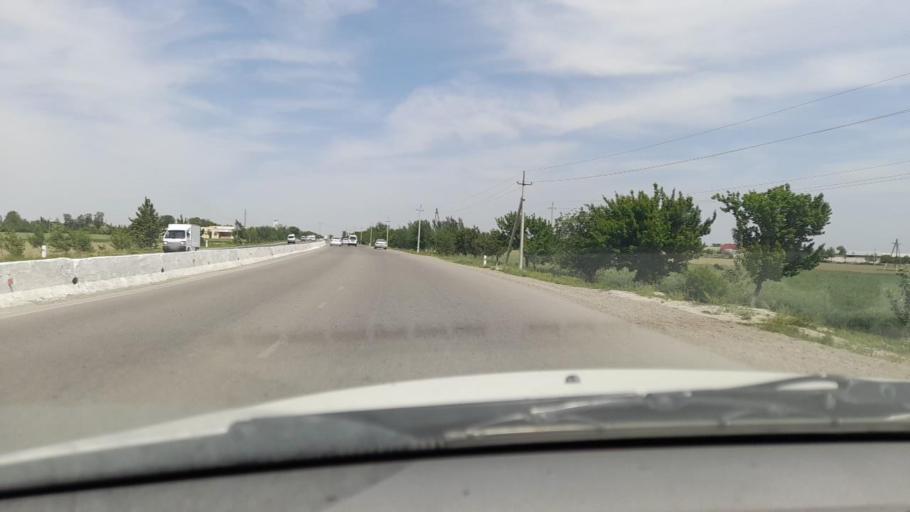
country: UZ
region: Bukhara
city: Wobkent
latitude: 40.0338
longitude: 64.5388
